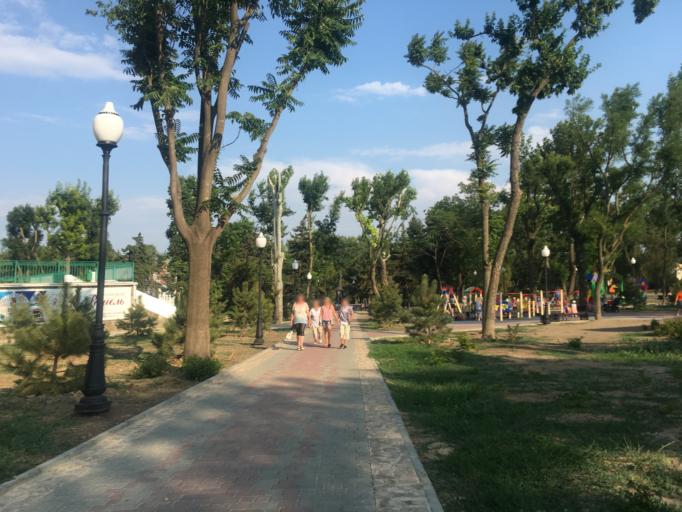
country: RU
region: Krasnodarskiy
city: Yeysk
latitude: 46.7144
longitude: 38.2745
